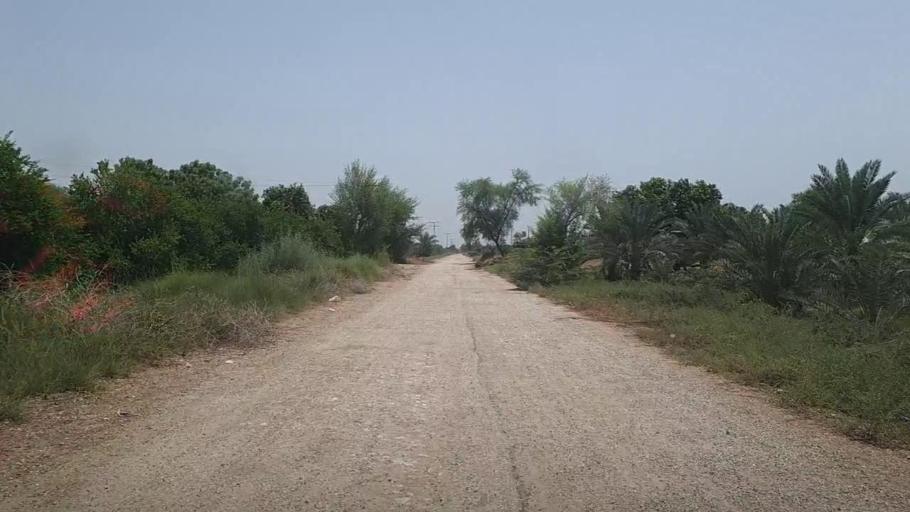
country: PK
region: Sindh
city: Pad Idan
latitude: 26.8523
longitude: 68.3247
